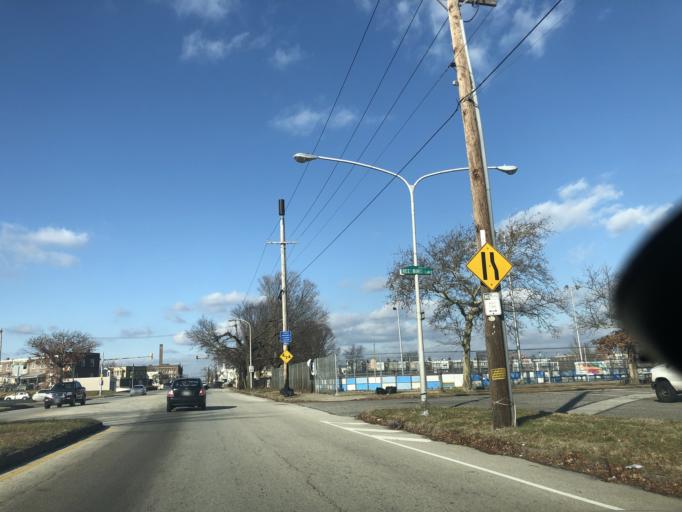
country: US
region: Pennsylvania
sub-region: Delaware County
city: Colwyn
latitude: 39.9131
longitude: -75.2324
